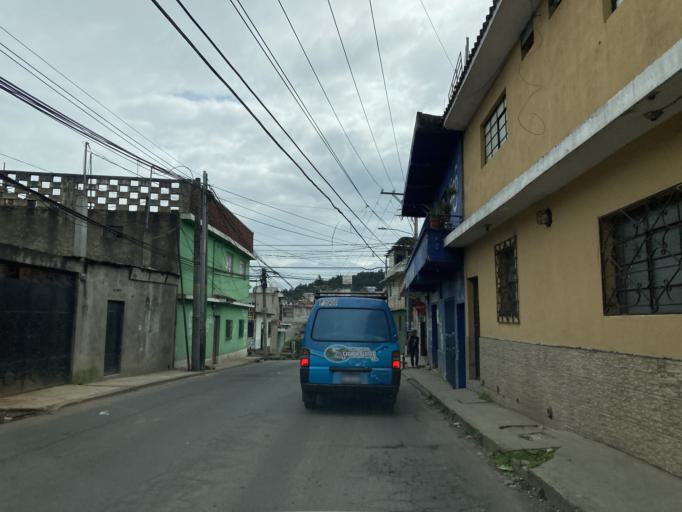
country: GT
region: Guatemala
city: San Jose Pinula
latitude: 14.5392
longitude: -90.4068
